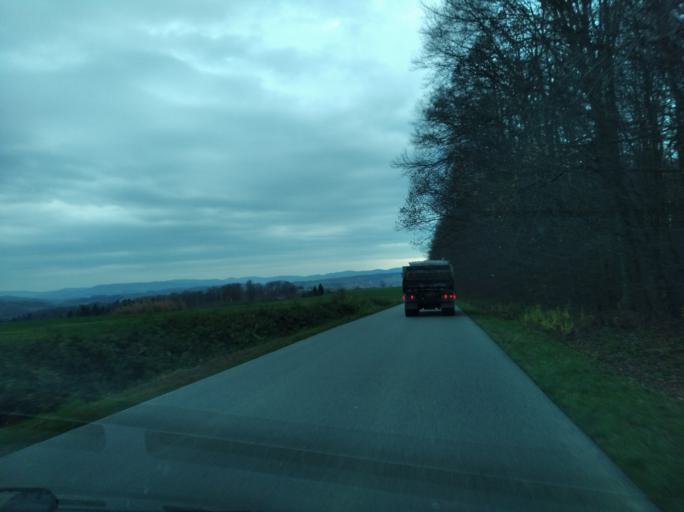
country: PL
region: Subcarpathian Voivodeship
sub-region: Powiat ropczycko-sedziszowski
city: Zagorzyce
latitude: 49.9452
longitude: 21.6938
